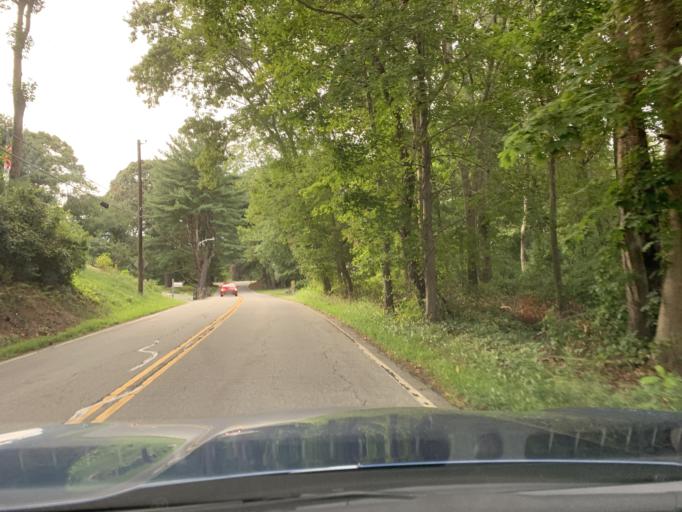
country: US
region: Rhode Island
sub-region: Kent County
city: East Greenwich
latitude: 41.6238
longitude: -71.4470
